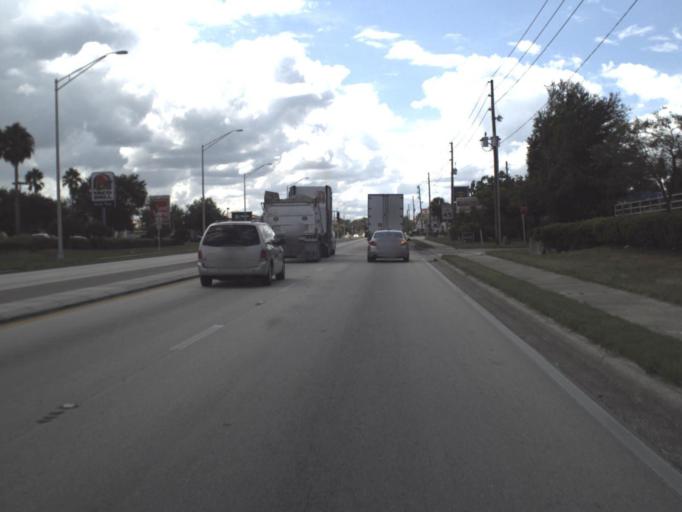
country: US
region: Florida
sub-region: Polk County
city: Lake Wales
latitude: 27.8942
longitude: -81.5566
